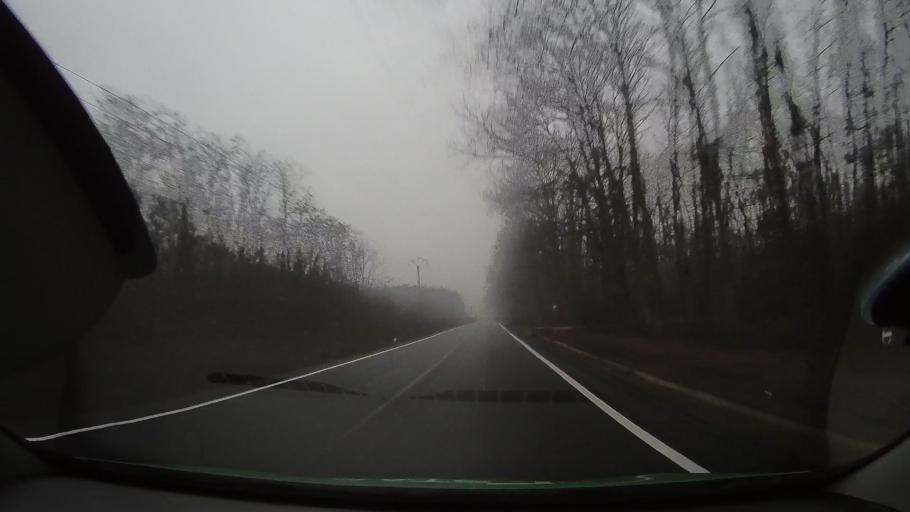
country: RO
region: Bihor
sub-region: Comuna Olcea
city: Olcea
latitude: 46.6991
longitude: 21.9647
